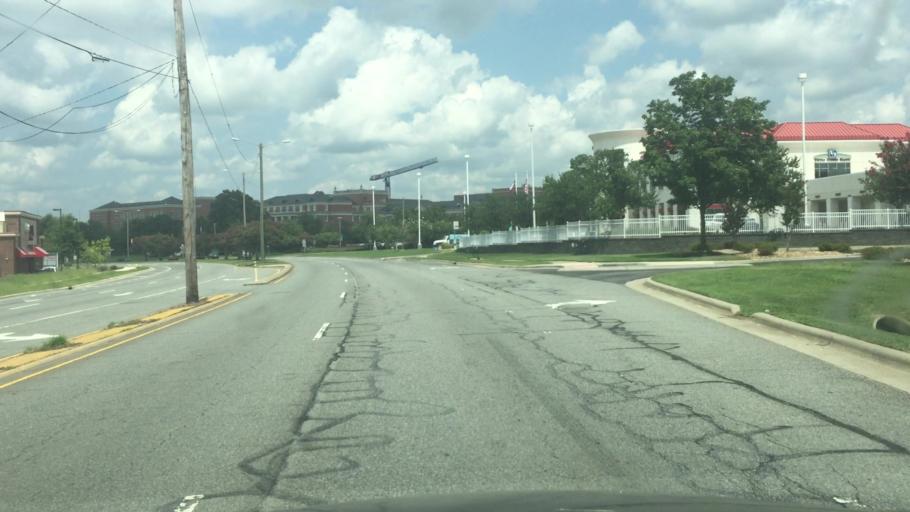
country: US
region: North Carolina
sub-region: Cabarrus County
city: Concord
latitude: 35.4328
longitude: -80.6041
